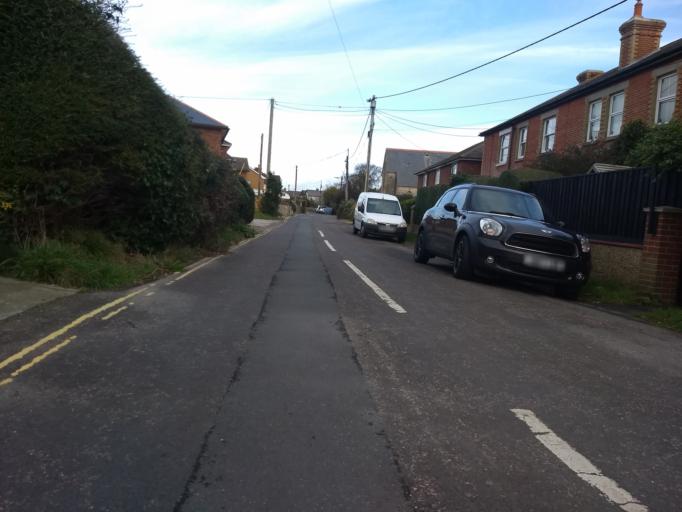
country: GB
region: England
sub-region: Isle of Wight
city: Freshwater
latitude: 50.6734
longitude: -1.5171
